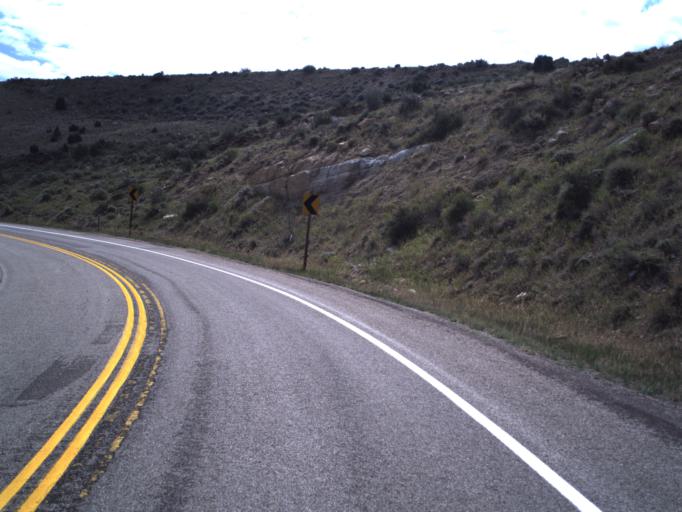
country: US
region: Utah
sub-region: Daggett County
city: Manila
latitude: 40.9086
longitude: -109.7006
